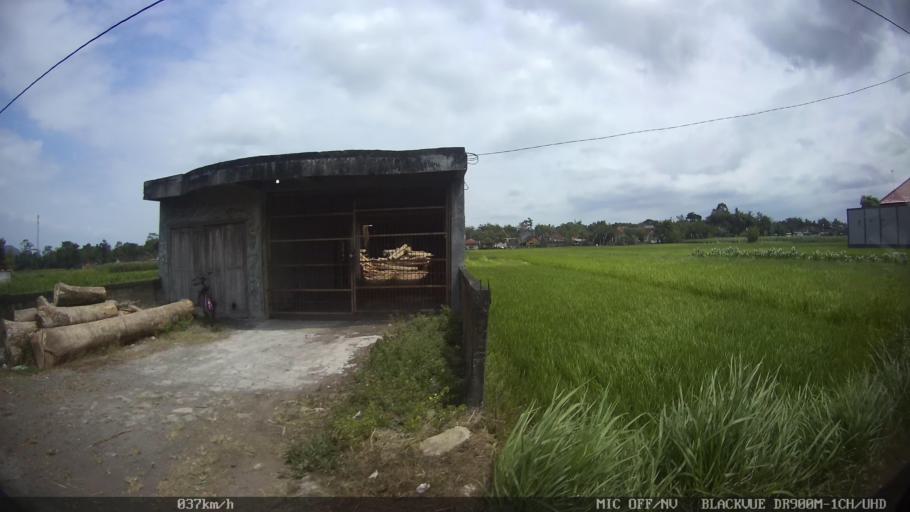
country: ID
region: Central Java
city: Candi Prambanan
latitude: -7.8136
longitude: 110.4998
